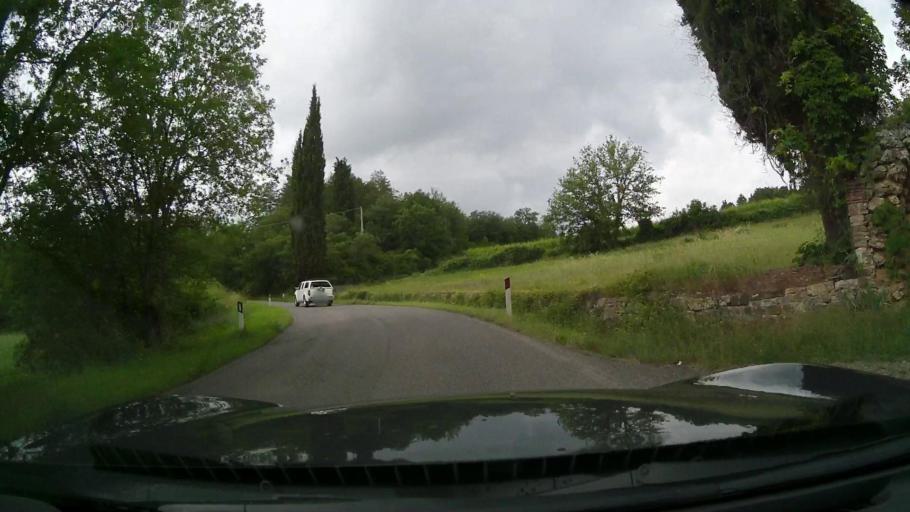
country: IT
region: Tuscany
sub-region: Province of Florence
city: Panzano in Chianti
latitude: 43.5272
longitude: 11.2892
